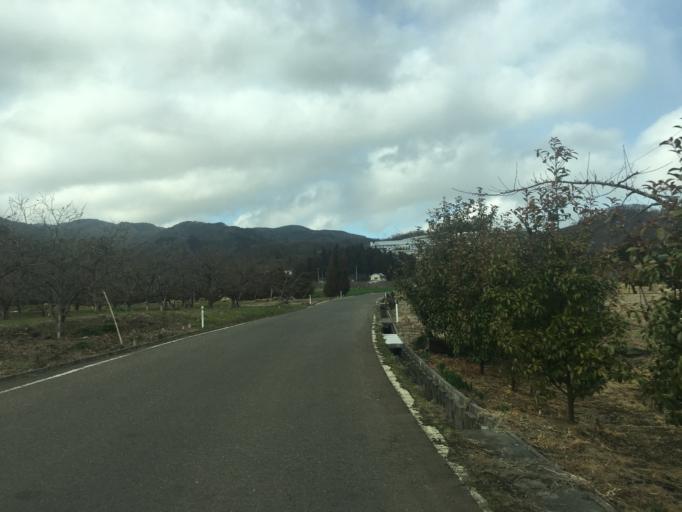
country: JP
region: Fukushima
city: Yanagawamachi-saiwaicho
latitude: 37.8906
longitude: 140.5822
